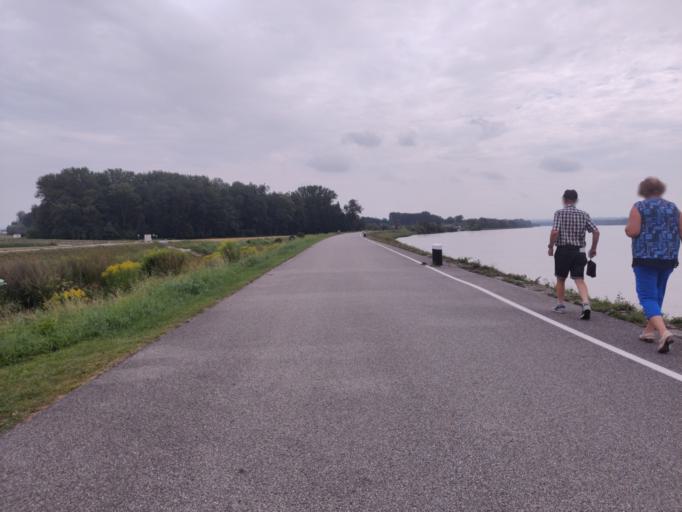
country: AT
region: Upper Austria
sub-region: Politischer Bezirk Perg
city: Perg
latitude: 48.2233
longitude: 14.5875
